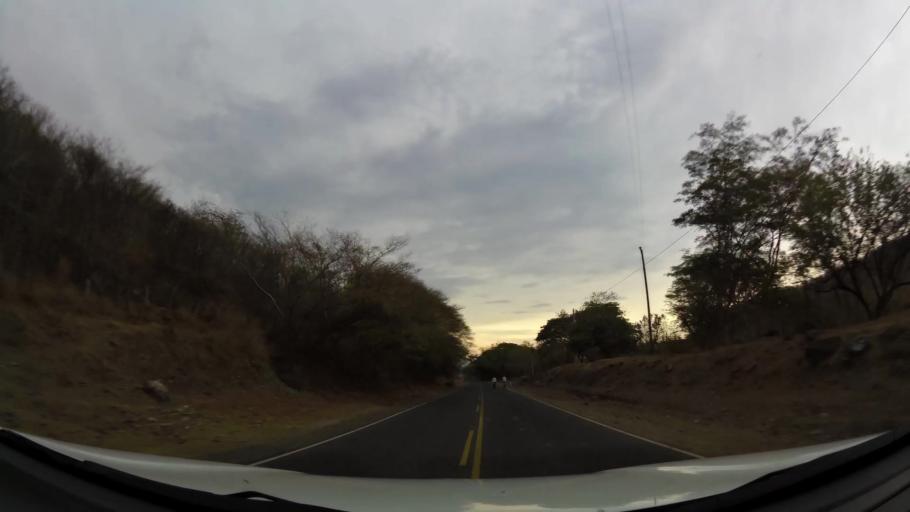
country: NI
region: Leon
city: La Jicaral
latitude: 12.7036
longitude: -86.3985
